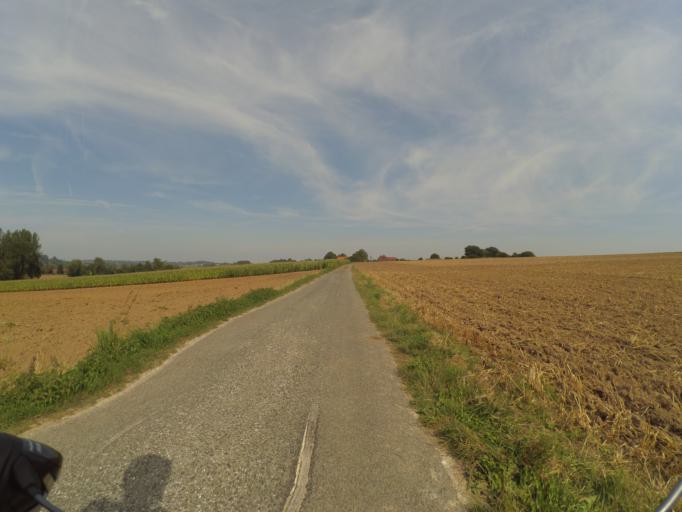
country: BE
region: Wallonia
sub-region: Province du Hainaut
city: Ellezelles
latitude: 50.7155
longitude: 3.7004
